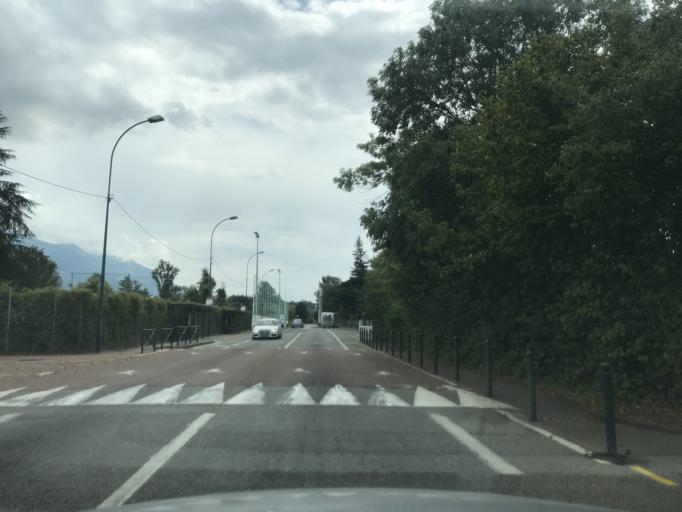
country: FR
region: Rhone-Alpes
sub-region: Departement de la Savoie
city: Brison-Saint-Innocent
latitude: 45.7033
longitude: 5.8911
